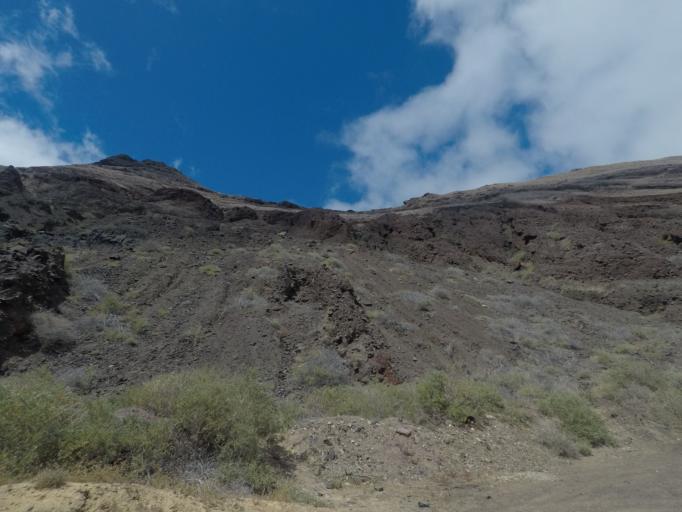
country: PT
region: Madeira
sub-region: Porto Santo
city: Vila de Porto Santo
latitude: 33.0624
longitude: -16.3030
